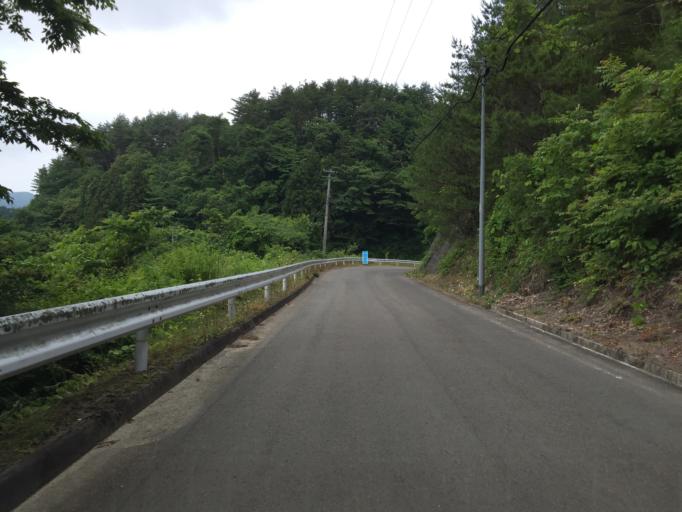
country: JP
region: Miyagi
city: Marumori
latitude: 37.8117
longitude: 140.7395
